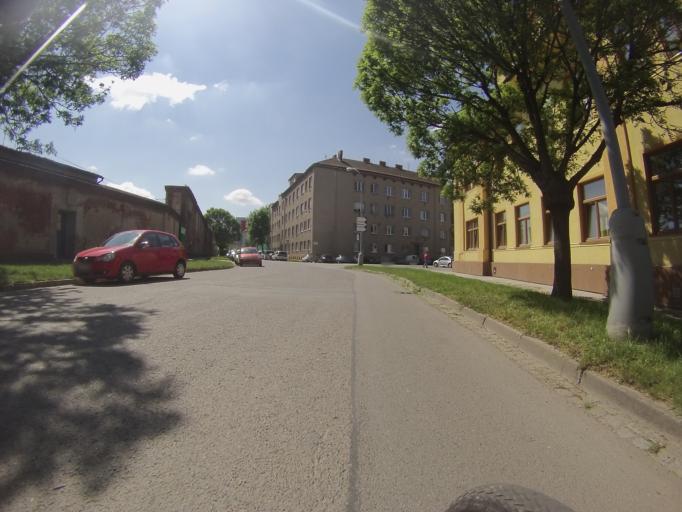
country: CZ
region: South Moravian
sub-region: Mesto Brno
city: Brno
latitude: 49.1804
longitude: 16.6193
